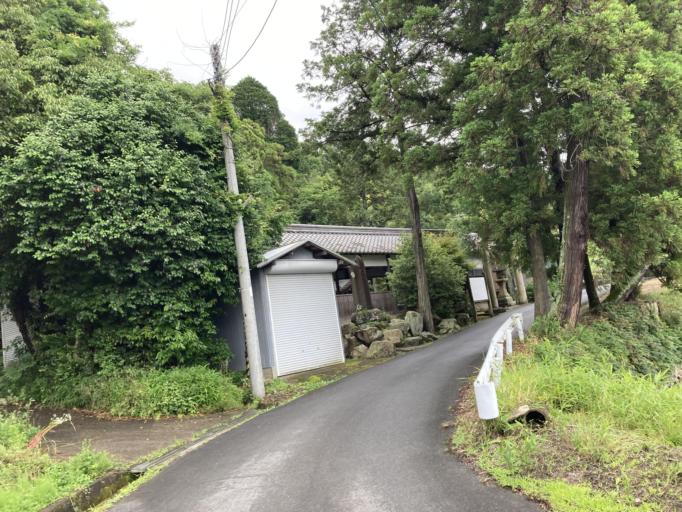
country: JP
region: Nara
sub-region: Ikoma-shi
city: Ikoma
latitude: 34.6241
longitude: 135.7110
